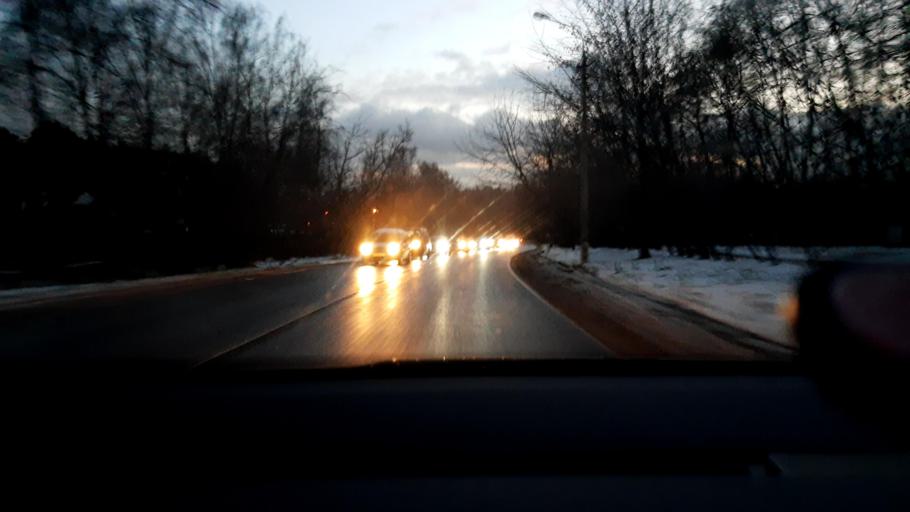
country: RU
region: Moskovskaya
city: Saltykovka
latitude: 55.7757
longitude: 37.9597
